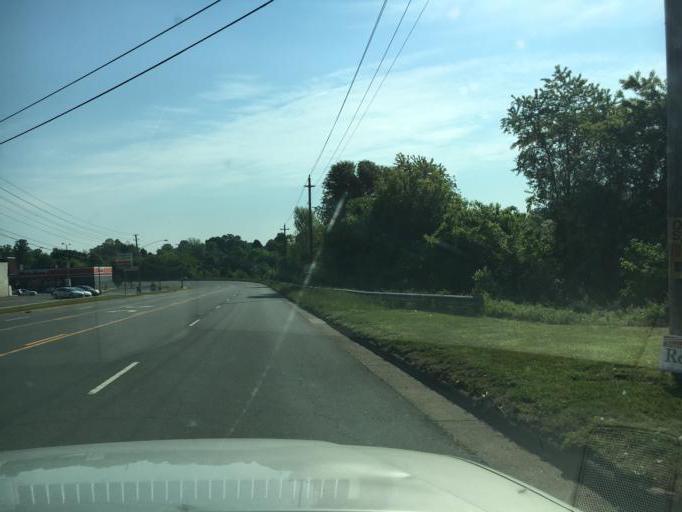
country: US
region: North Carolina
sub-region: Burke County
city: Morganton
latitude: 35.7353
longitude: -81.6822
